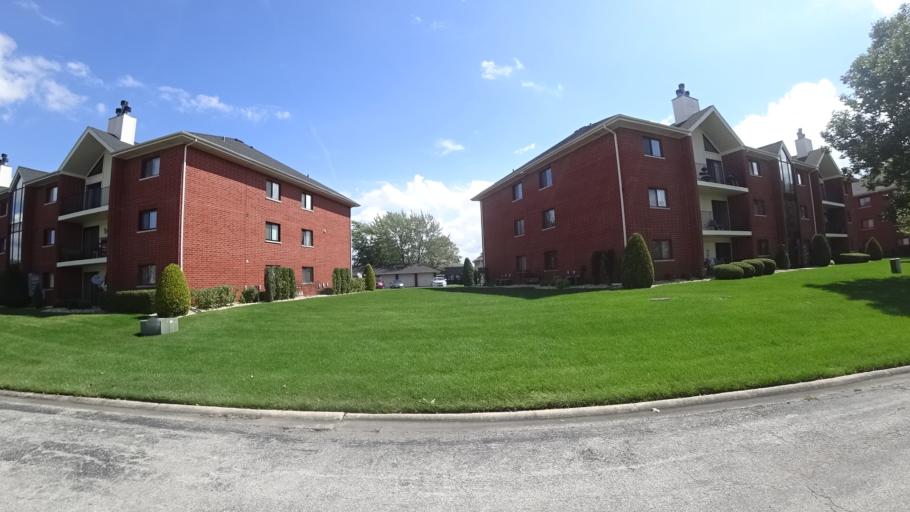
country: US
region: Illinois
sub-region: Cook County
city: Tinley Park
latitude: 41.5618
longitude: -87.7787
